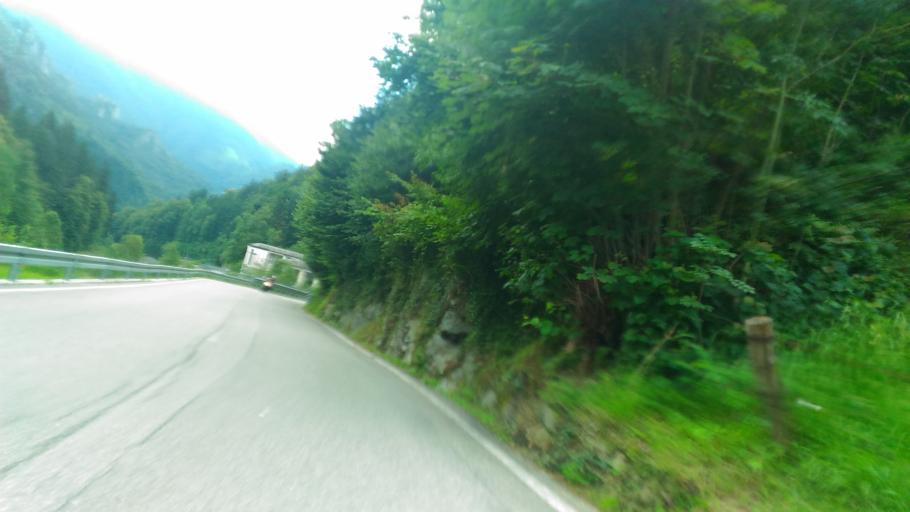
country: IT
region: Lombardy
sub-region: Provincia di Bergamo
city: Mezzoldo
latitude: 46.0094
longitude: 9.6672
